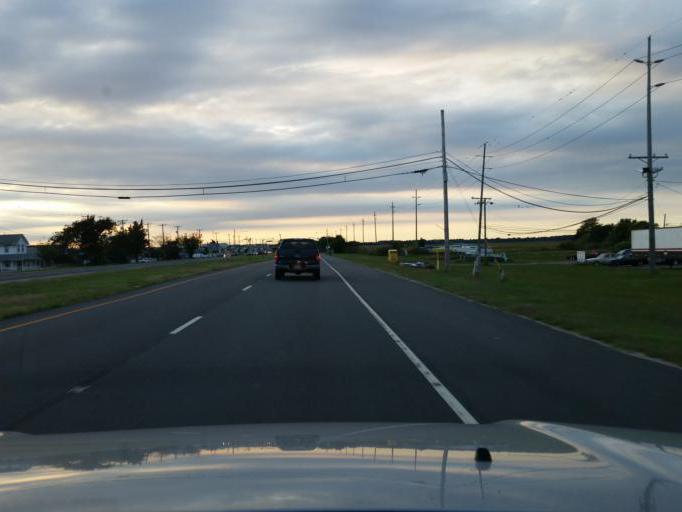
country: US
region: New Jersey
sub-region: Cape May County
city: Wildwood Crest
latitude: 38.9936
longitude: -74.8398
